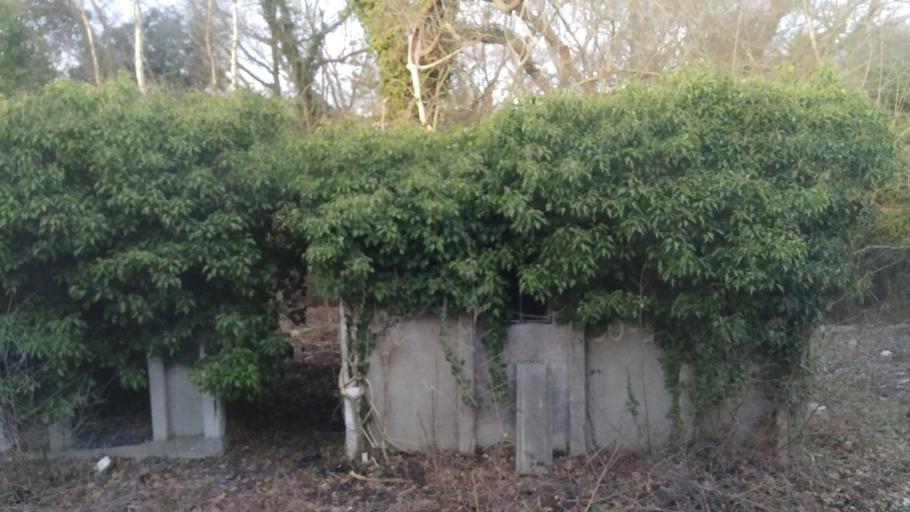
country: GB
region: England
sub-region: Kent
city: Lenham
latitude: 51.1566
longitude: 0.7457
